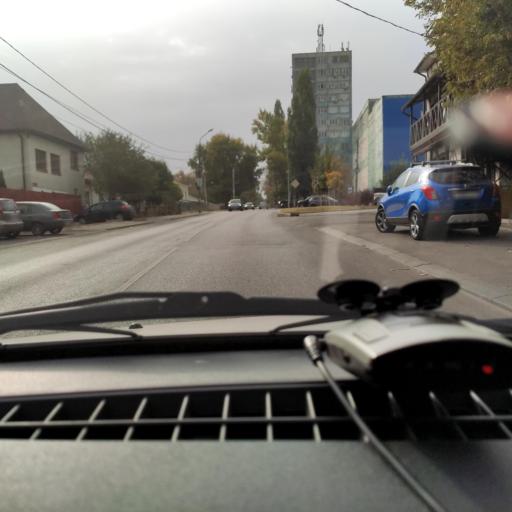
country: RU
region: Voronezj
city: Voronezh
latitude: 51.6916
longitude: 39.1903
